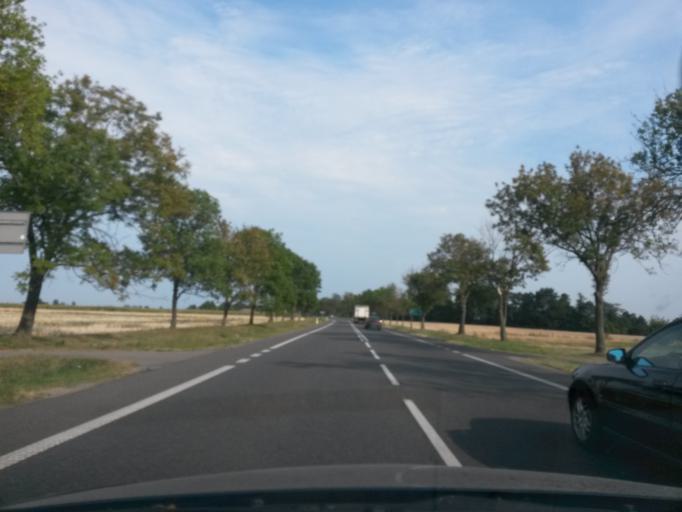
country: PL
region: Masovian Voivodeship
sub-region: Powiat sierpecki
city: Rosciszewo
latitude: 52.8269
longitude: 19.7613
